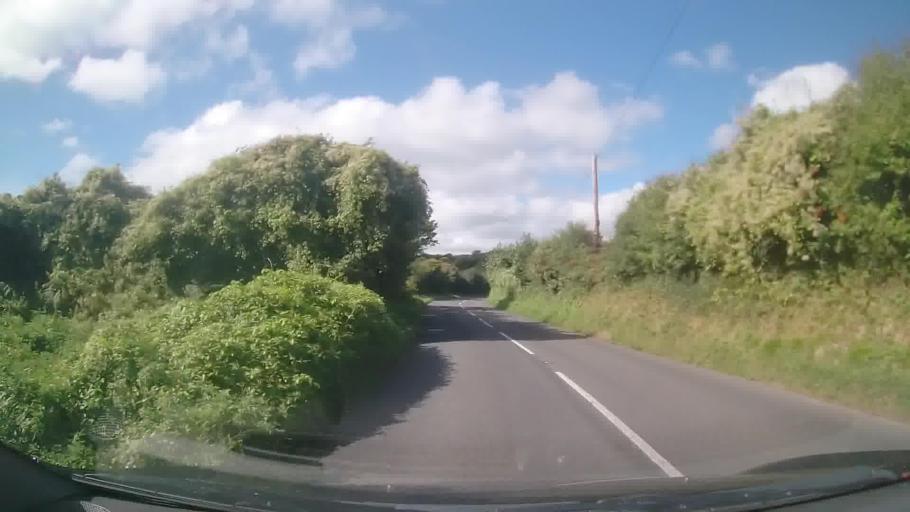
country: GB
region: Wales
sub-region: Pembrokeshire
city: Penally
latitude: 51.6559
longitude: -4.7378
